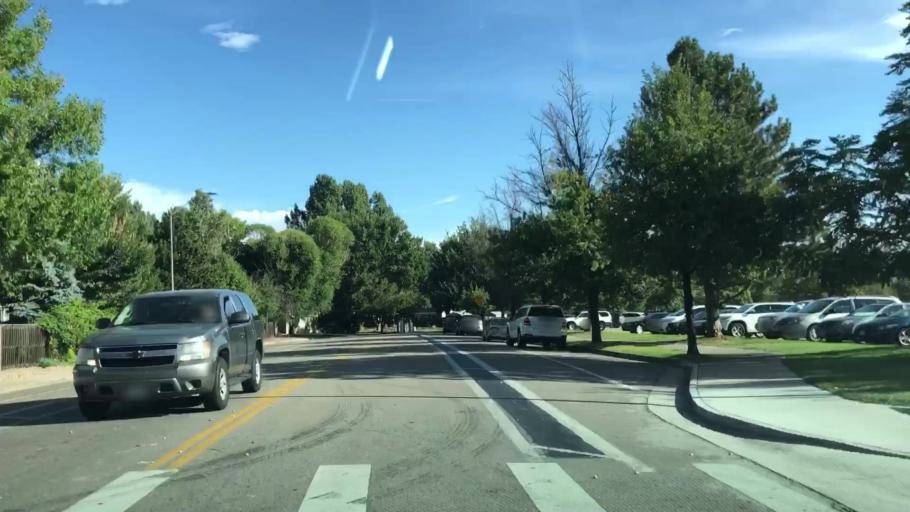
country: US
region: Colorado
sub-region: Larimer County
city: Fort Collins
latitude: 40.5258
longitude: -105.0488
